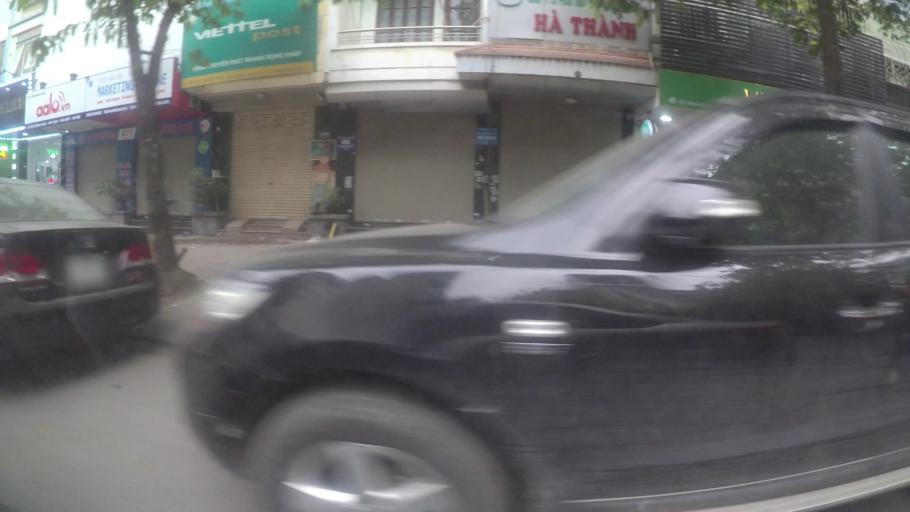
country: VN
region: Ha Noi
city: Cau Dien
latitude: 21.0352
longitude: 105.7731
